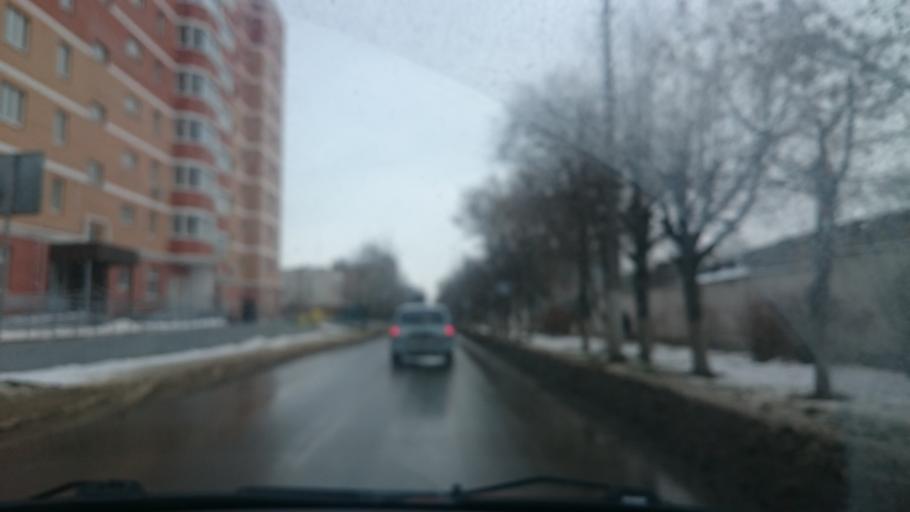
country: RU
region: Tula
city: Tula
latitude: 54.2093
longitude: 37.6147
